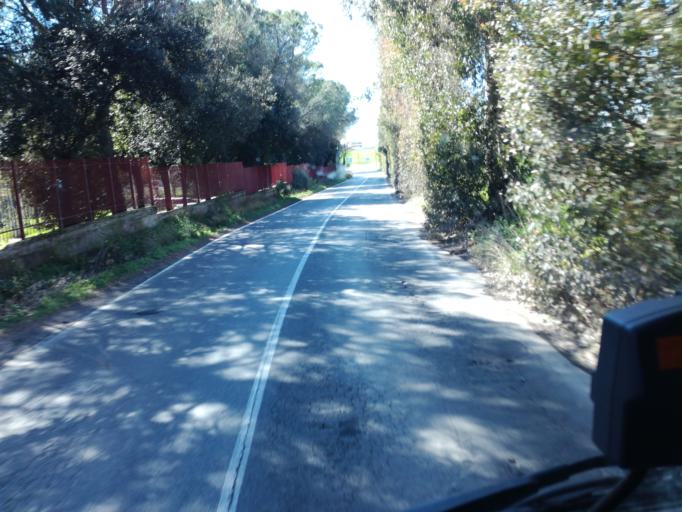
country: IT
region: Latium
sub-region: Citta metropolitana di Roma Capitale
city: Area Produttiva
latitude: 41.6974
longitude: 12.5327
